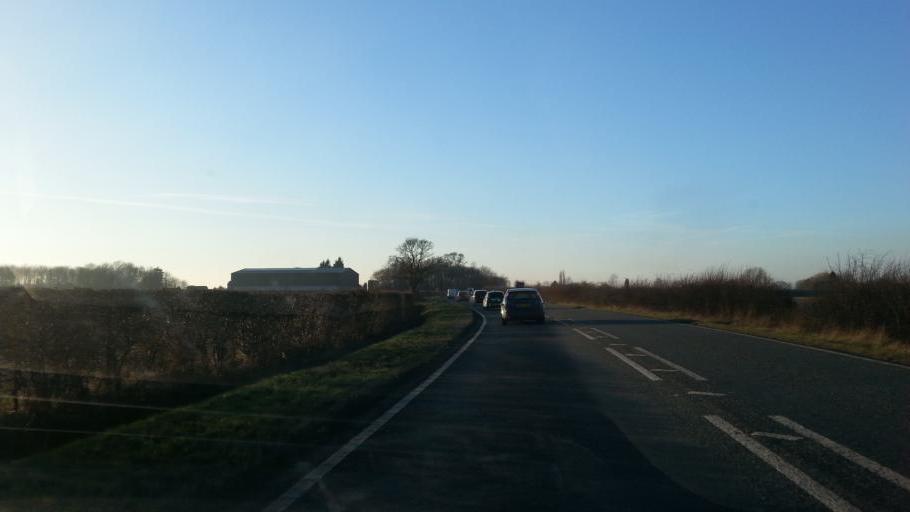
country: GB
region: England
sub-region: Lincolnshire
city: Navenby
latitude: 53.0653
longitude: -0.6160
